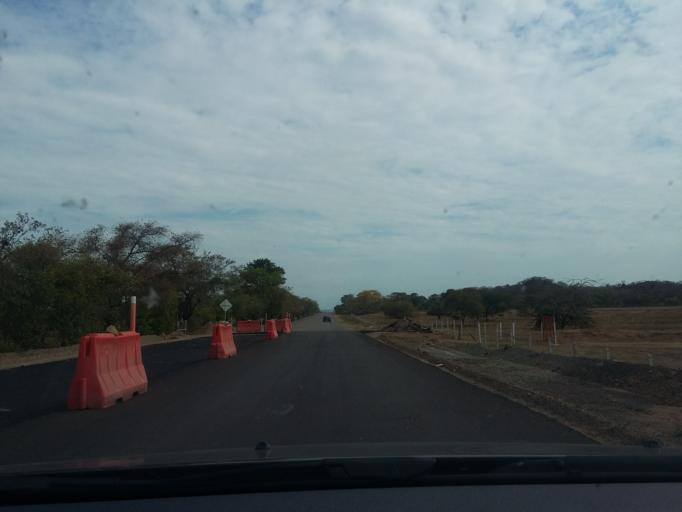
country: CO
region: Tolima
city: Ambalema
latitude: 4.6807
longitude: -74.7869
